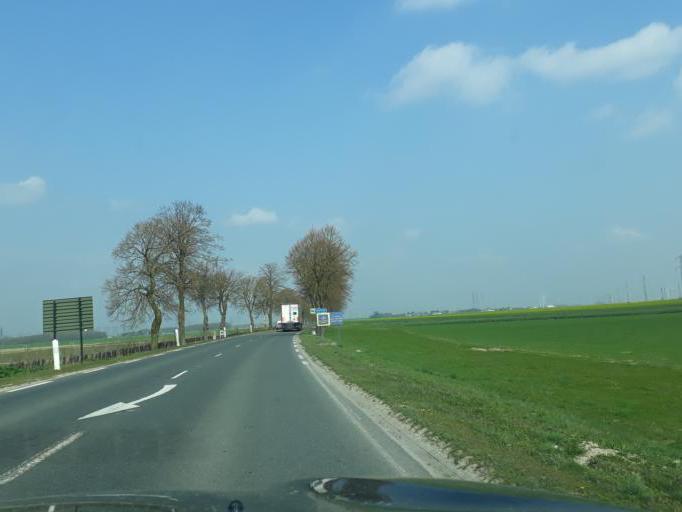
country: FR
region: Centre
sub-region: Departement du Loiret
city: Artenay
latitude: 48.0888
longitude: 1.8656
